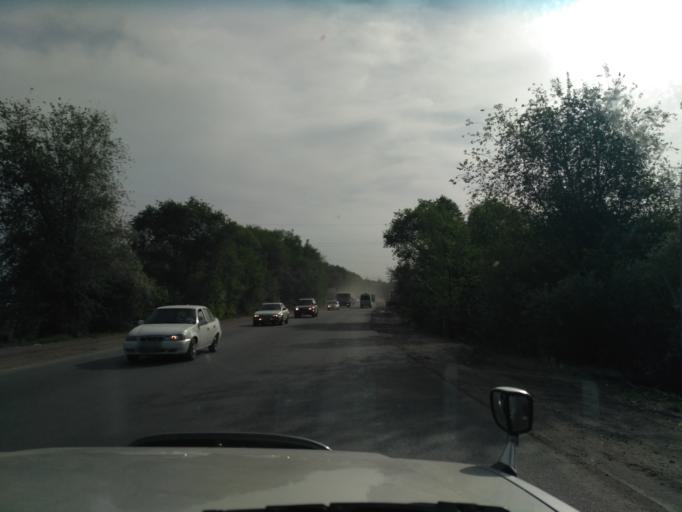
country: KZ
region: Almaty Oblysy
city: Burunday
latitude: 43.2215
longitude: 76.6520
